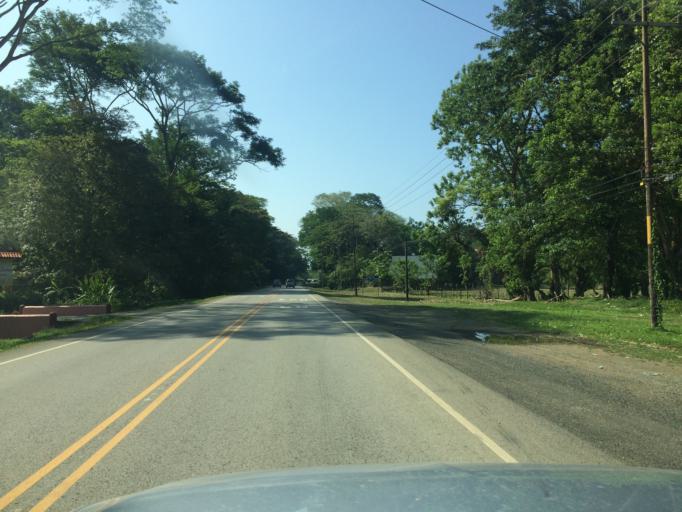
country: CR
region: San Jose
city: San Isidro
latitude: 9.2534
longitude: -83.8603
